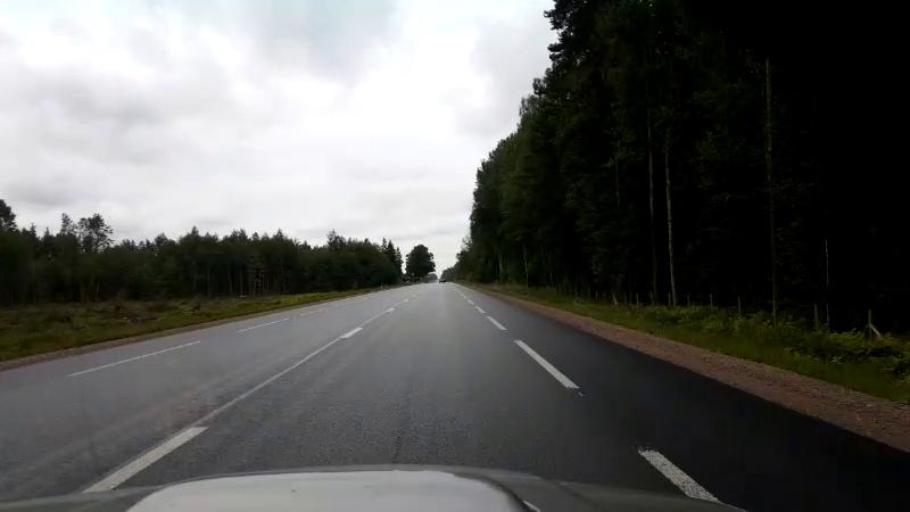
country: LV
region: Lecava
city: Iecava
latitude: 56.6946
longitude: 24.2420
